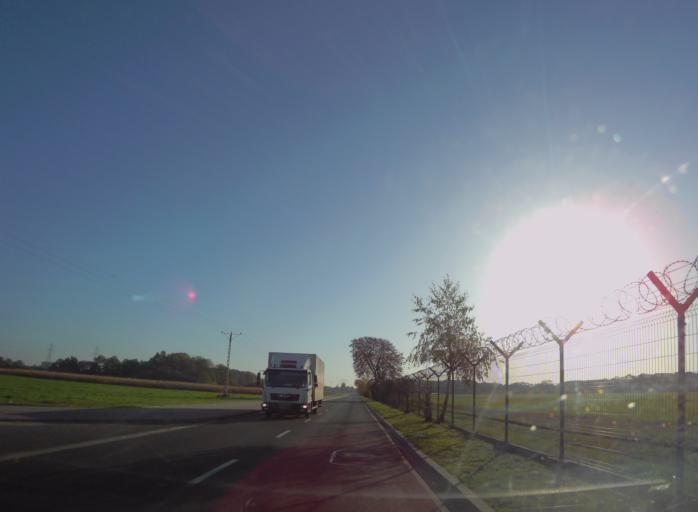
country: PL
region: Masovian Voivodeship
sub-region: Powiat pruszkowski
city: Otrebusy
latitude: 52.1537
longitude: 20.7692
